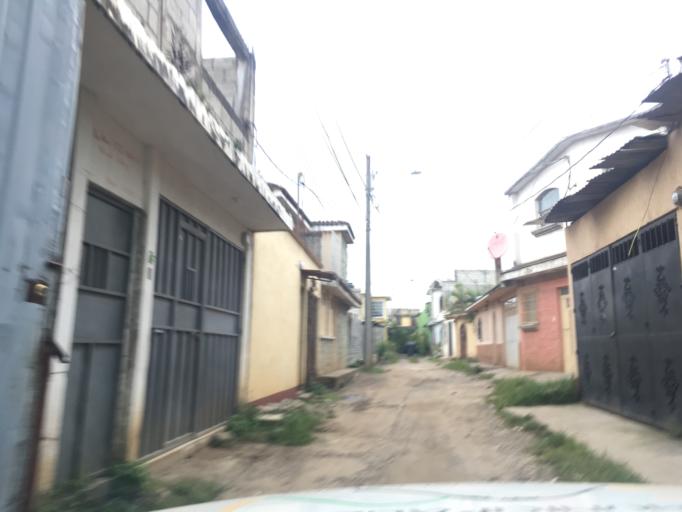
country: GT
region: Guatemala
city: Petapa
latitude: 14.5024
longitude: -90.5663
